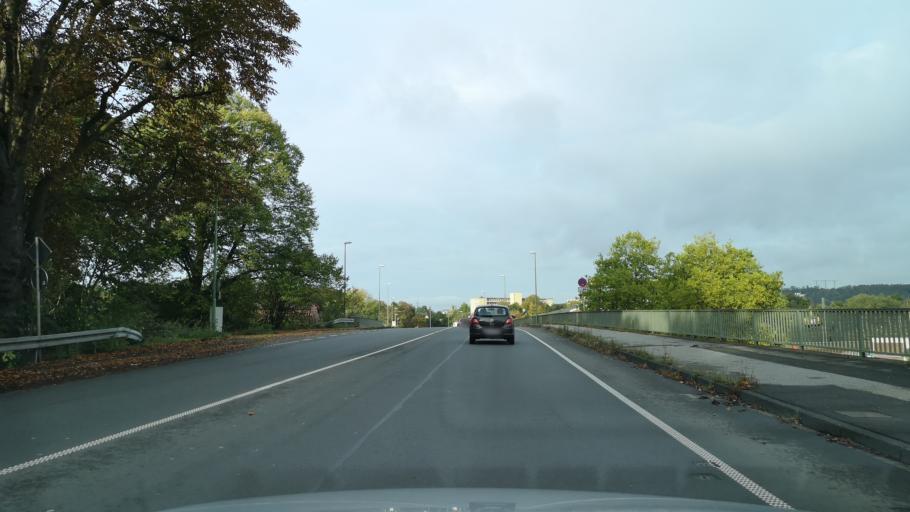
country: DE
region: North Rhine-Westphalia
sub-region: Regierungsbezirk Arnsberg
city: Hagen
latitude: 51.4046
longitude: 7.4892
